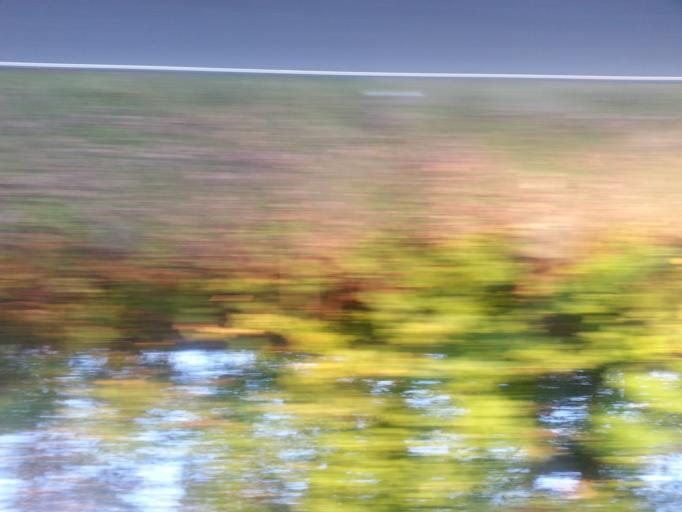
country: US
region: Tennessee
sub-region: Campbell County
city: Hunter
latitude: 36.3546
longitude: -84.1478
